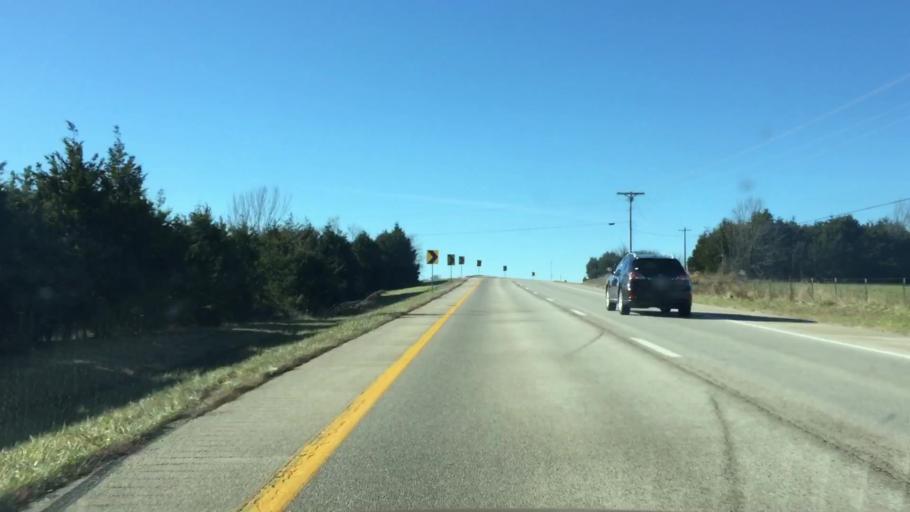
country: US
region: Missouri
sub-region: Cole County
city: Wardsville
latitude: 38.4249
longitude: -92.3286
